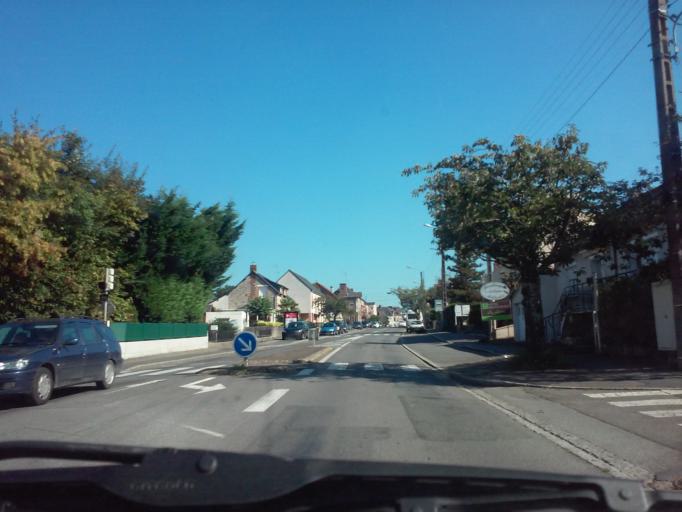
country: FR
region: Brittany
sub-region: Departement d'Ille-et-Vilaine
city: Betton
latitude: 48.1788
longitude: -1.6386
